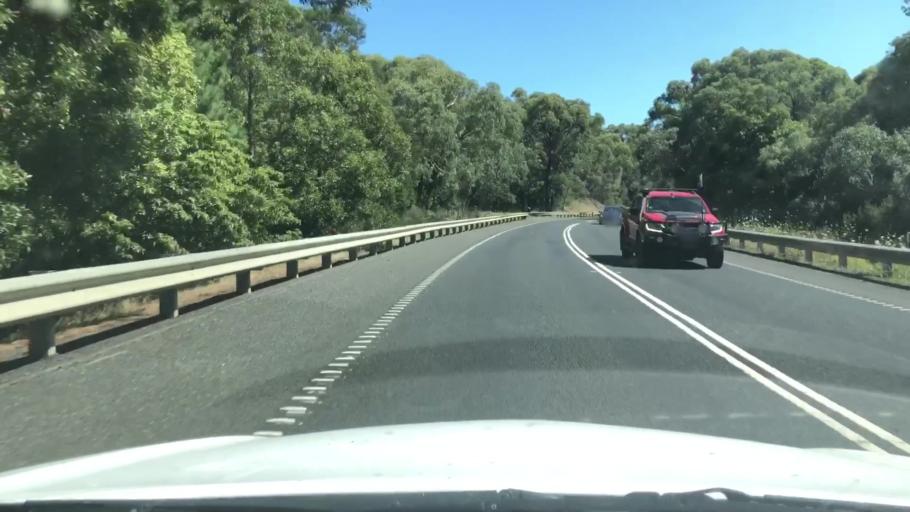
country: AU
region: Victoria
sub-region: Yarra Ranges
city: Selby
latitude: -37.9531
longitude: 145.3852
